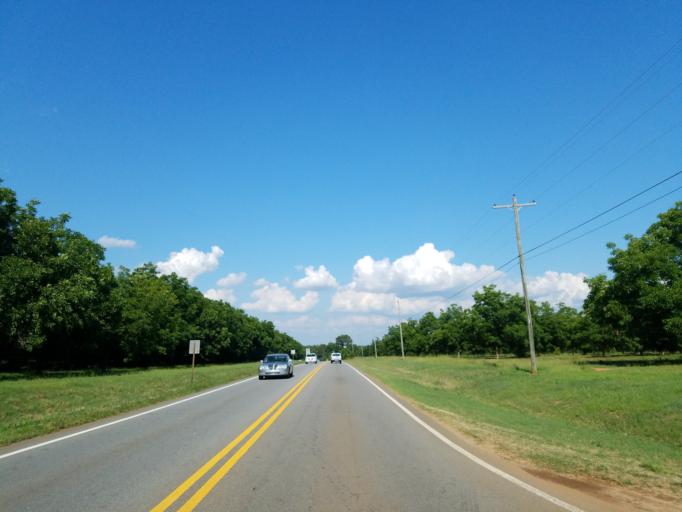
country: US
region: Georgia
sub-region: Peach County
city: Fort Valley
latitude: 32.5540
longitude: -83.8693
